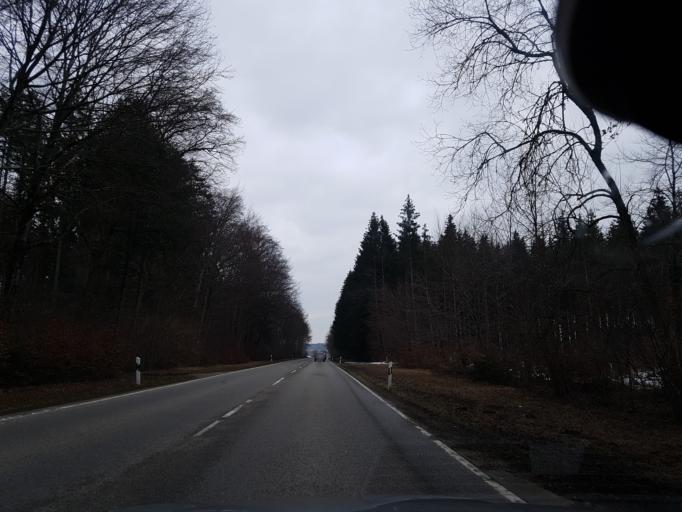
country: DE
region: Bavaria
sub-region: Upper Bavaria
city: Aying
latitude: 47.9760
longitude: 11.7484
